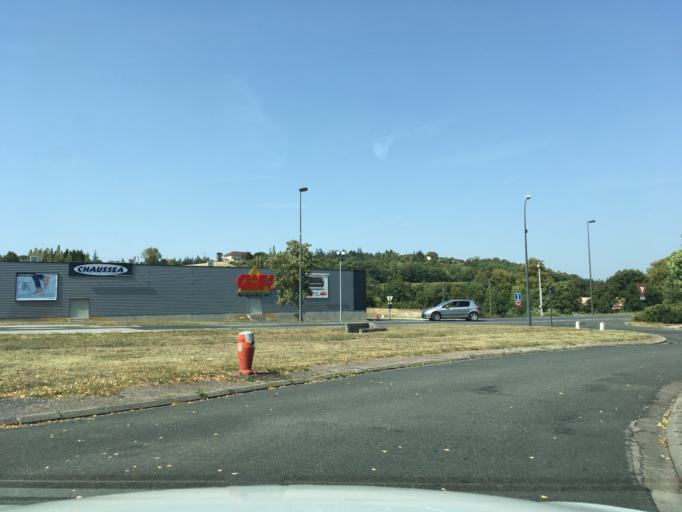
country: FR
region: Midi-Pyrenees
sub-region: Departement du Tarn
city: Castres
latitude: 43.5938
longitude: 2.2660
